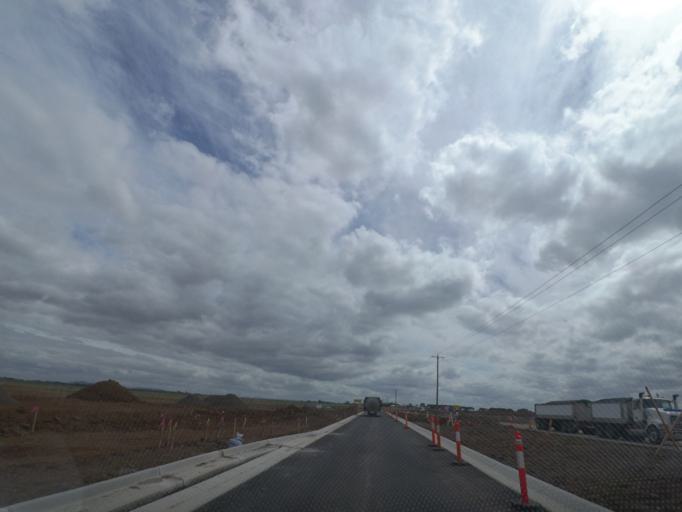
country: AU
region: Victoria
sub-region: Wyndham
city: Tarneit
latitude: -37.8432
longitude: 144.6396
